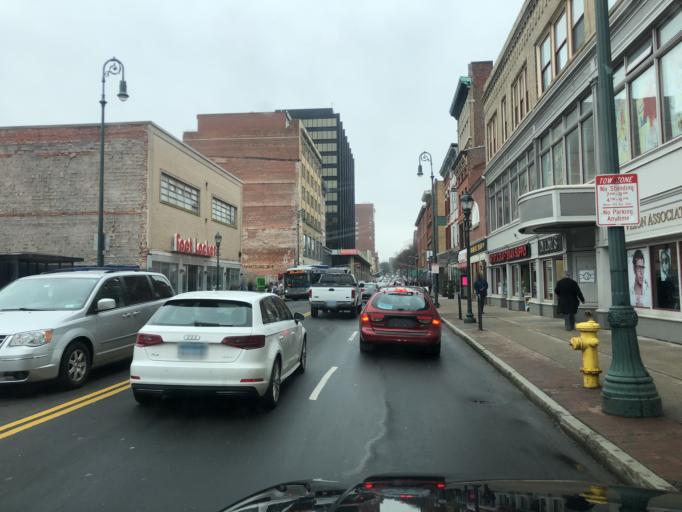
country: US
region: Connecticut
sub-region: New Haven County
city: New Haven
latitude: 41.3055
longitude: -72.9244
